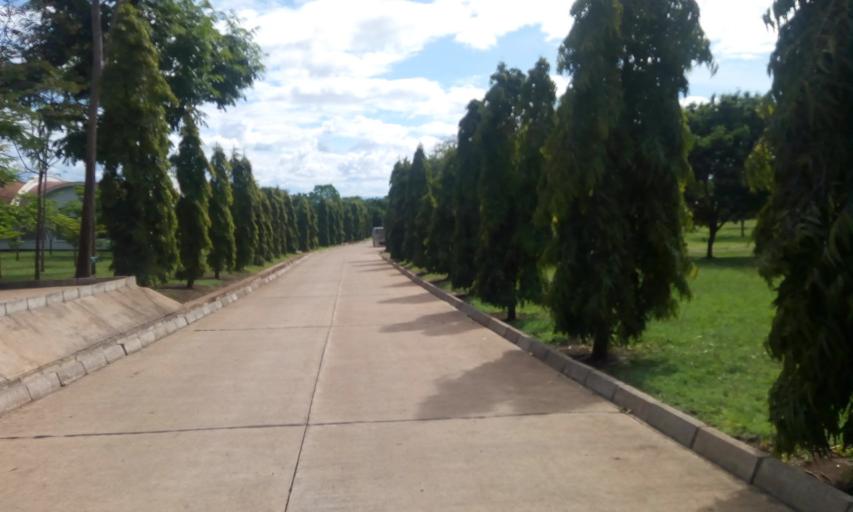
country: TZ
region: Arusha
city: Usa River
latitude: -3.4003
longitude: 36.7969
